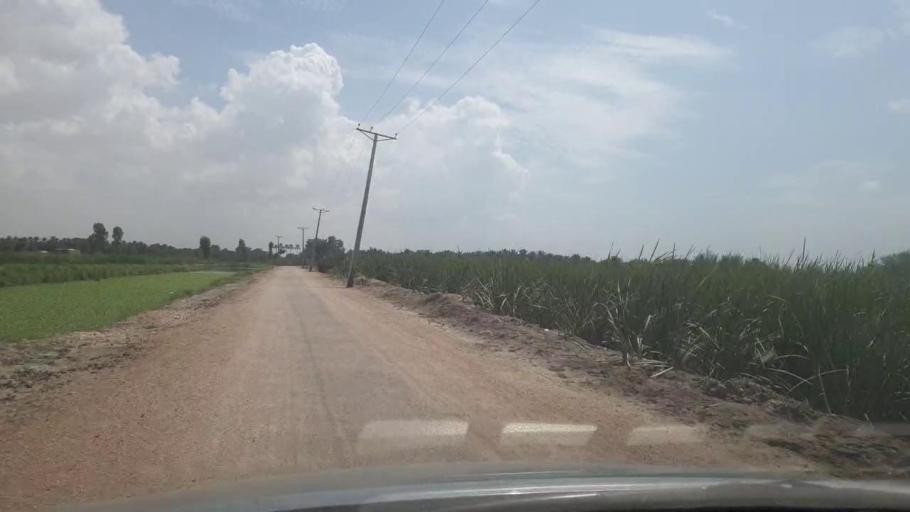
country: PK
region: Sindh
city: Khairpur
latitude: 27.4780
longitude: 68.8105
